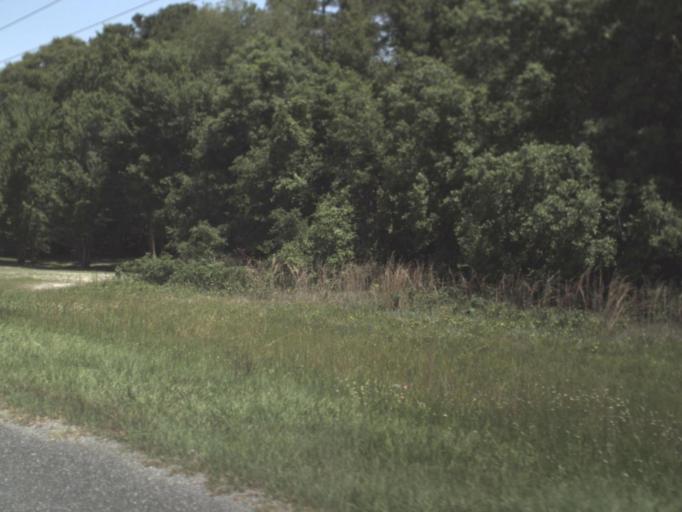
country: US
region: Florida
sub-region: Bradford County
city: Starke
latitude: 29.9519
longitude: -82.1466
